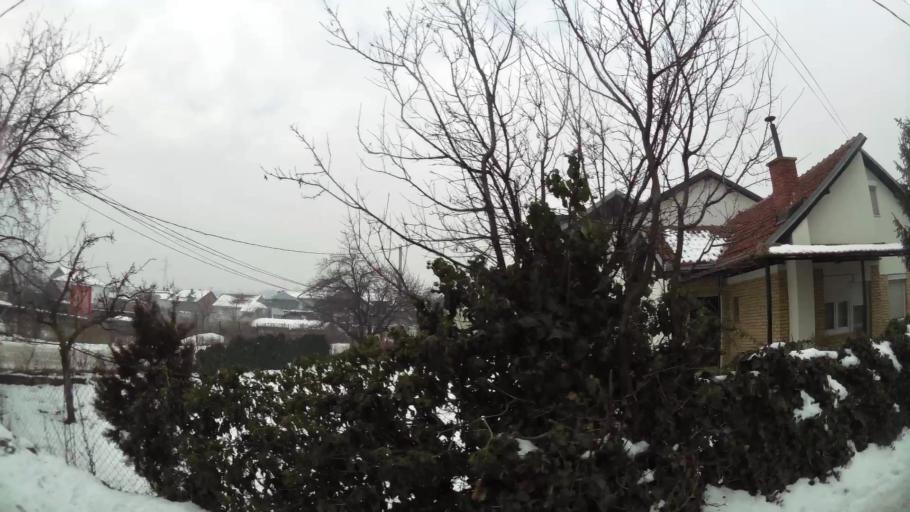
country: MK
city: Kondovo
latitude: 42.0424
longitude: 21.3506
